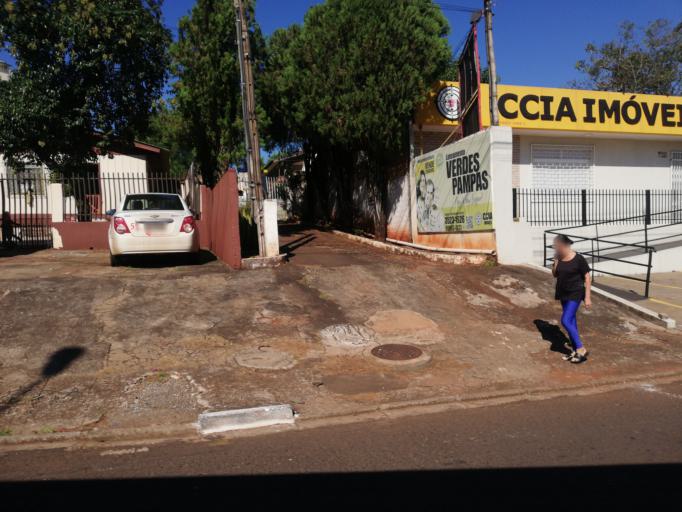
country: BR
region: Parana
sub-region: Foz Do Iguacu
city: Foz do Iguacu
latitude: -25.5489
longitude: -54.5763
